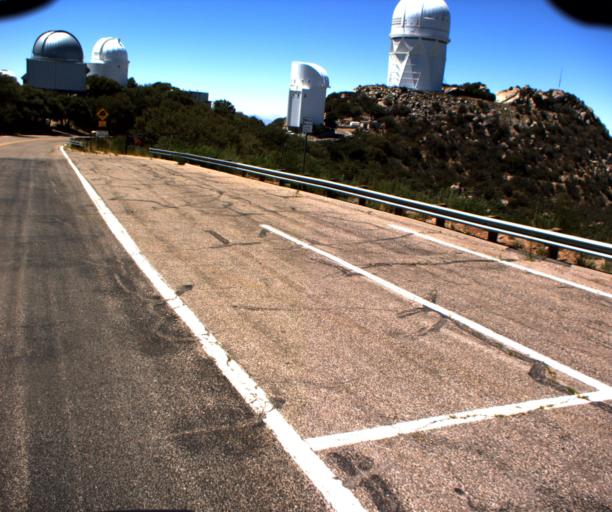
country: US
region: Arizona
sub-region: Pima County
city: Sells
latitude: 31.9609
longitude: -111.5989
